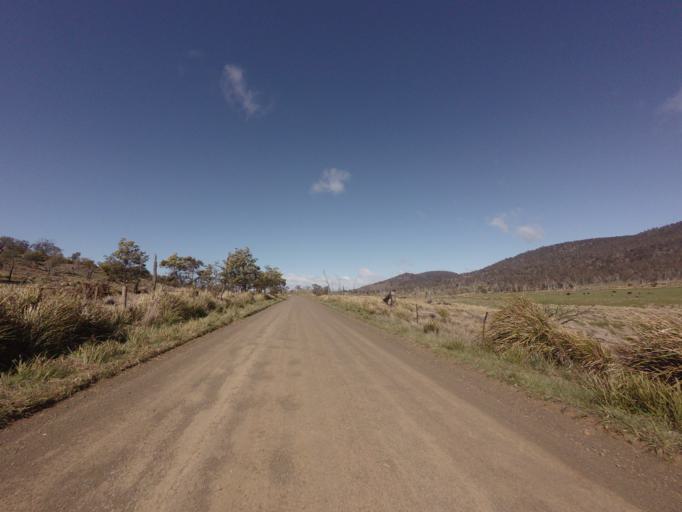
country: AU
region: Tasmania
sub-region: Northern Midlands
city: Evandale
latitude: -41.9343
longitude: 147.4185
